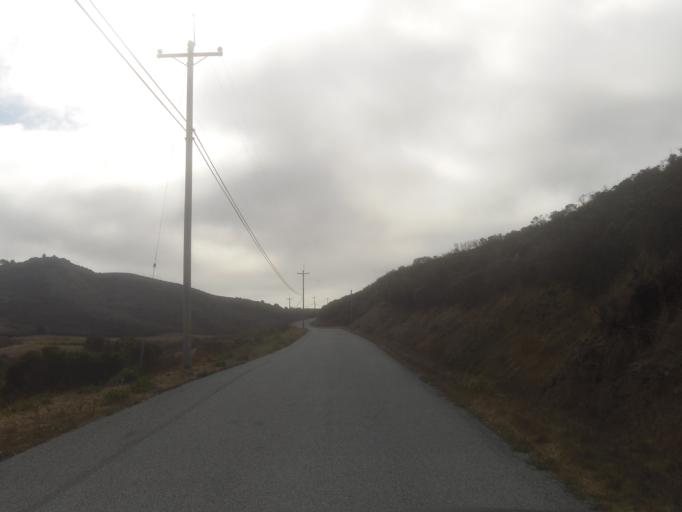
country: US
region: California
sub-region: San Mateo County
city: Half Moon Bay
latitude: 37.4100
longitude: -122.4052
